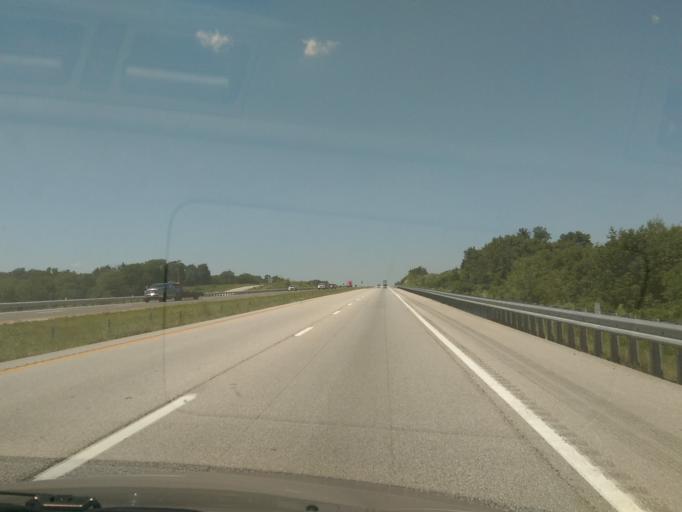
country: US
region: Missouri
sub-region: Cooper County
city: Boonville
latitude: 38.9377
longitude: -92.9818
